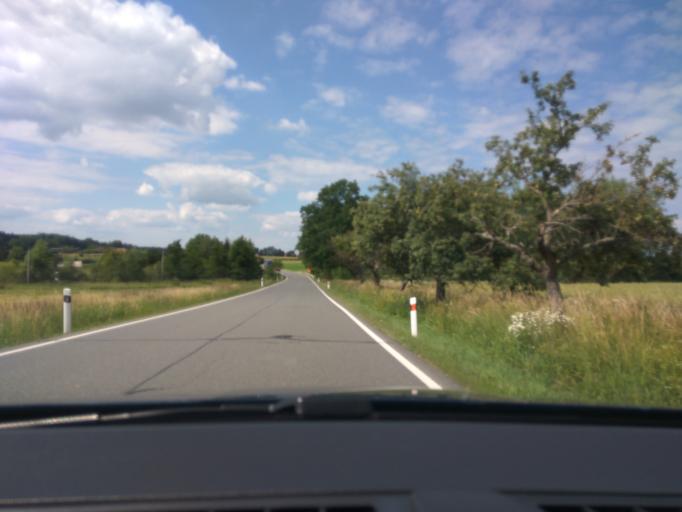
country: CZ
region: Jihocesky
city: Bernartice
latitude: 49.4026
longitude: 14.3631
